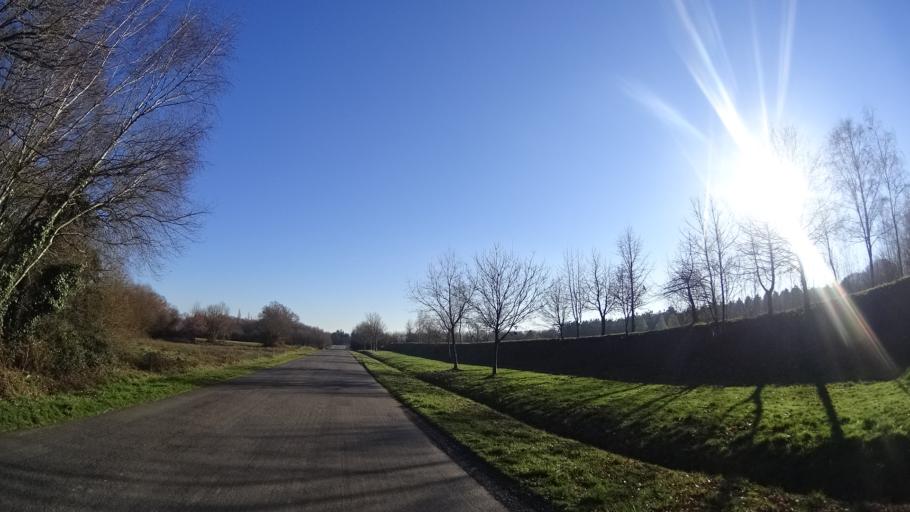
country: FR
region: Brittany
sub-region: Departement du Morbihan
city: Allaire
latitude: 47.6392
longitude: -2.1505
